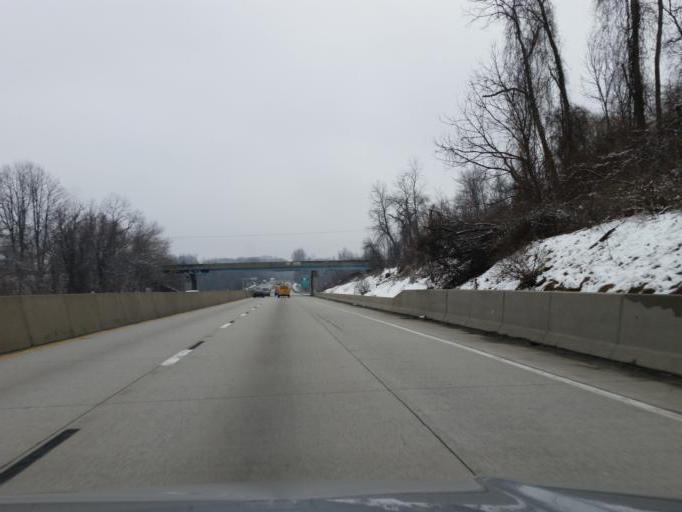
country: US
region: Pennsylvania
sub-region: Dauphin County
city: Steelton
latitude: 40.1913
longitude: -76.8495
